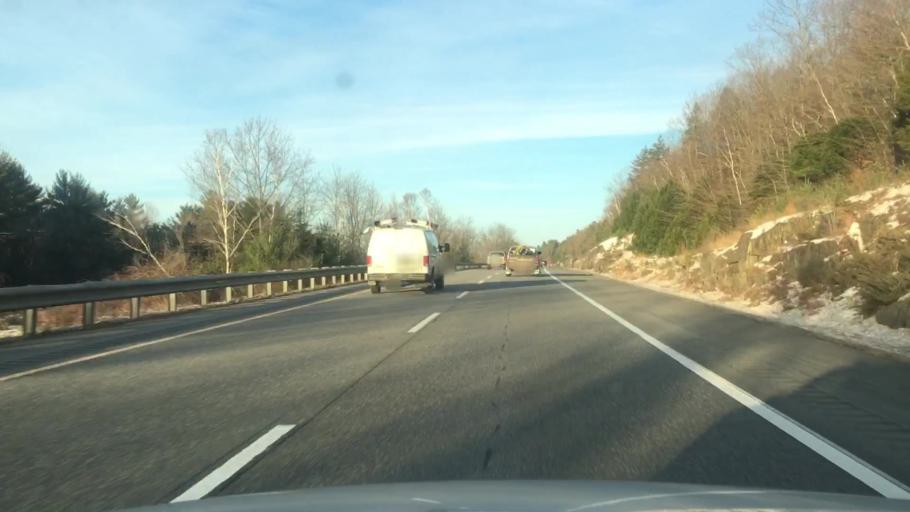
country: US
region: Maine
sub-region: Kennebec County
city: Sidney
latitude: 44.3782
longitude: -69.7692
